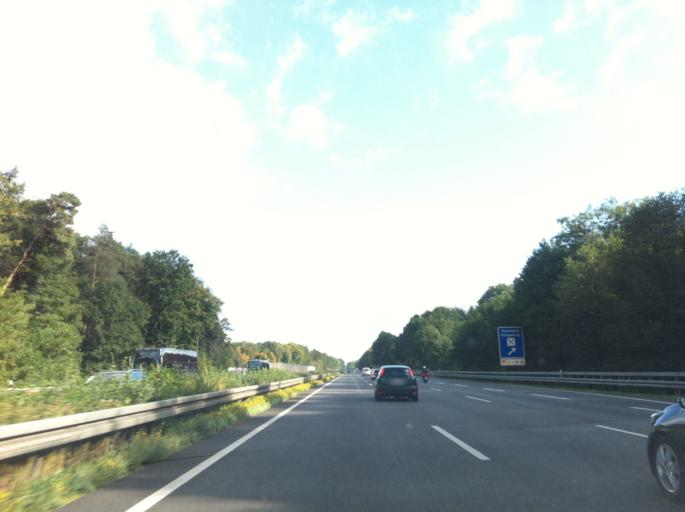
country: DE
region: North Rhine-Westphalia
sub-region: Regierungsbezirk Koln
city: Rosrath
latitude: 50.8998
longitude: 7.1472
